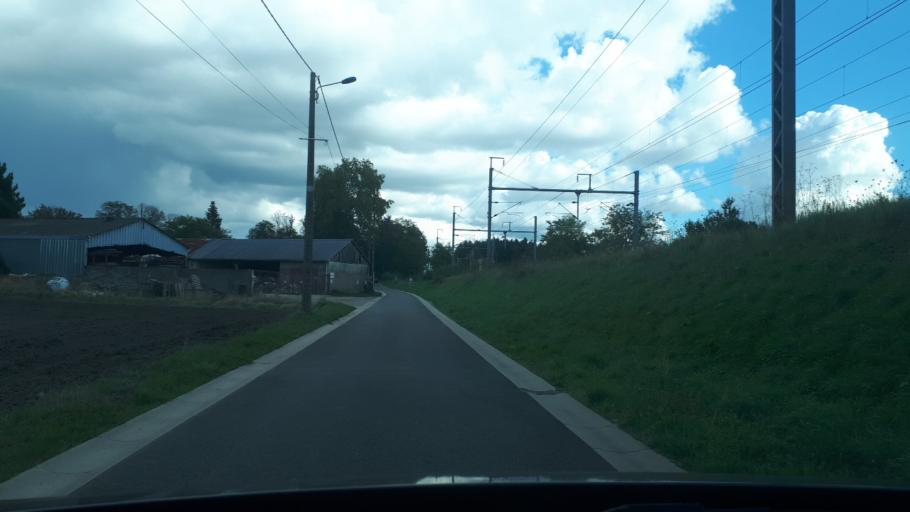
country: FR
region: Centre
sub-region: Departement du Loir-et-Cher
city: Noyers-sur-Cher
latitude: 47.2848
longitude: 1.3887
